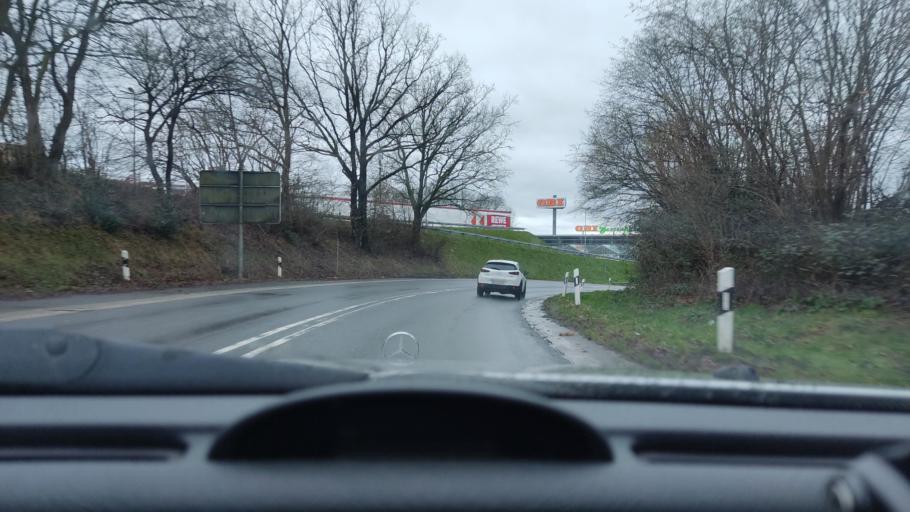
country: DE
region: North Rhine-Westphalia
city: Wermelskirchen
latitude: 51.1363
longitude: 7.1986
